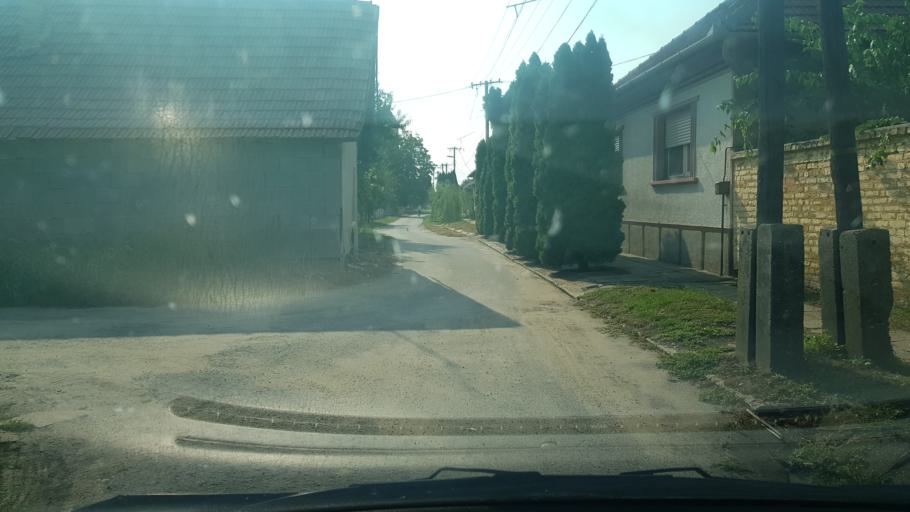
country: HU
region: Pest
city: Cegledbercel
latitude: 47.2240
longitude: 19.6670
